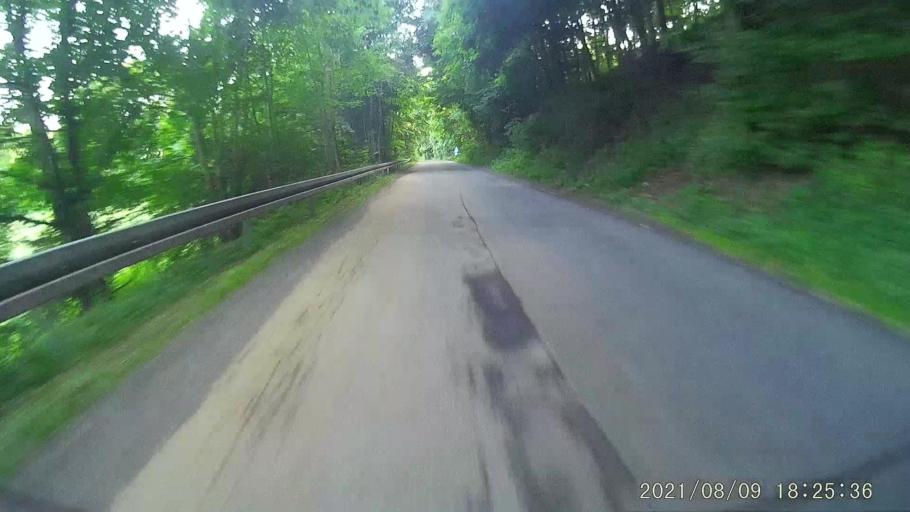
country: PL
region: Lower Silesian Voivodeship
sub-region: Powiat zabkowicki
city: Bardo
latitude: 50.5092
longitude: 16.7247
